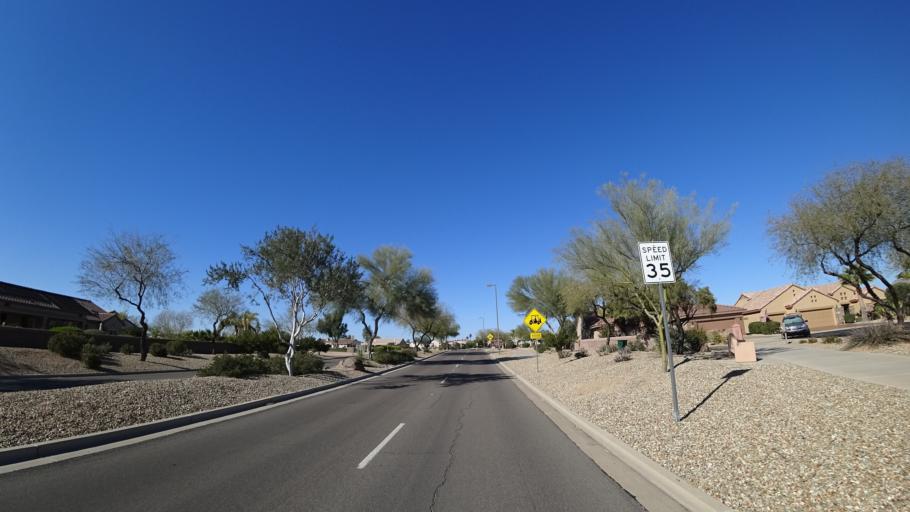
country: US
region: Arizona
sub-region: Maricopa County
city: Sun City West
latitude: 33.6513
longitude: -112.4128
